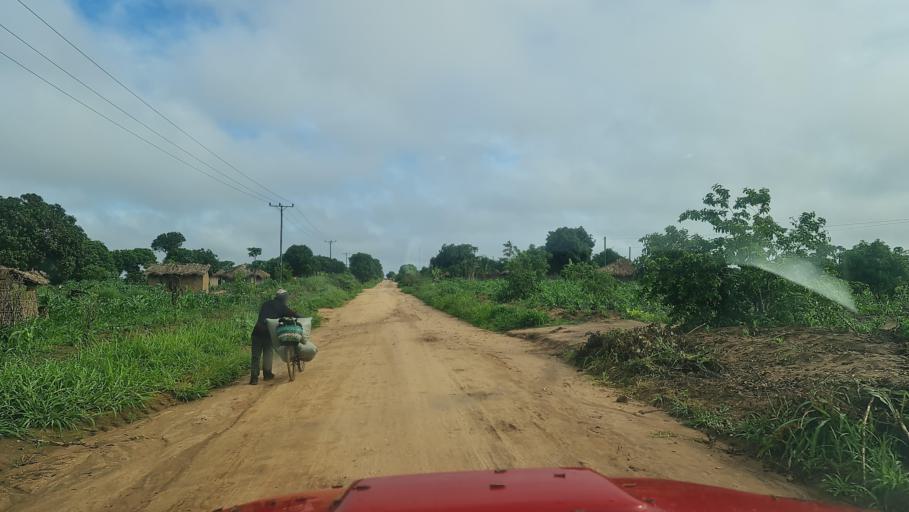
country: MW
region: Southern Region
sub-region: Nsanje District
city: Nsanje
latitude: -17.3084
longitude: 35.5929
